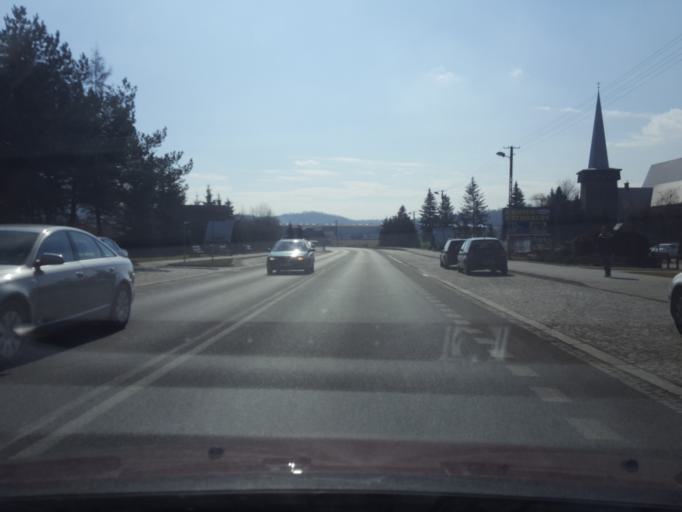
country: PL
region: Lesser Poland Voivodeship
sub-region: Powiat nowosadecki
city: Lososina Dolna
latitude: 49.7095
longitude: 20.6442
